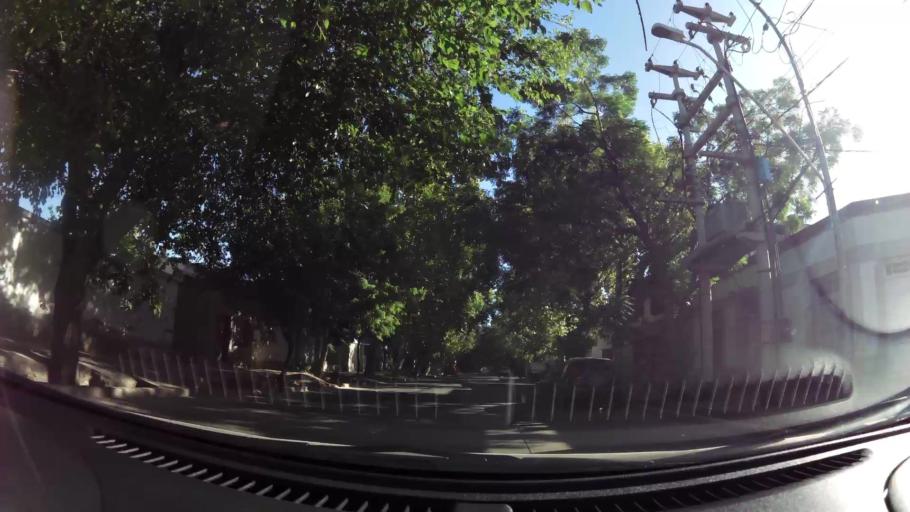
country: AR
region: Mendoza
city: Las Heras
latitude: -32.8668
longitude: -68.8358
